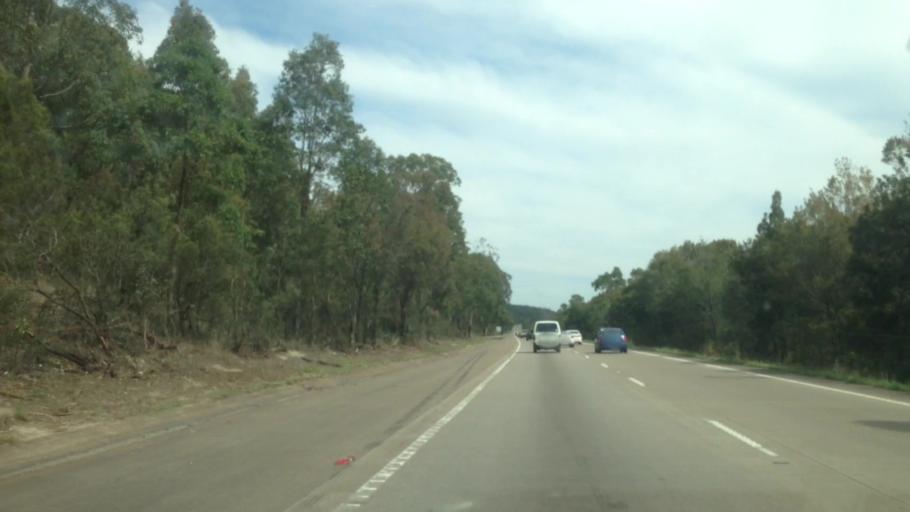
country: AU
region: New South Wales
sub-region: Lake Macquarie Shire
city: Fennell Bay
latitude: -32.9620
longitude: 151.5397
